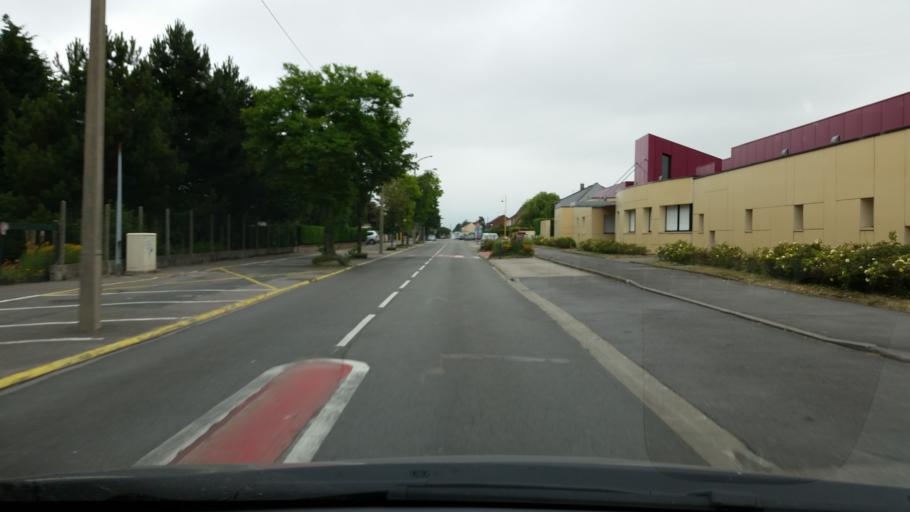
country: FR
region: Nord-Pas-de-Calais
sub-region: Departement du Pas-de-Calais
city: Marck
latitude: 50.9489
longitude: 1.9403
